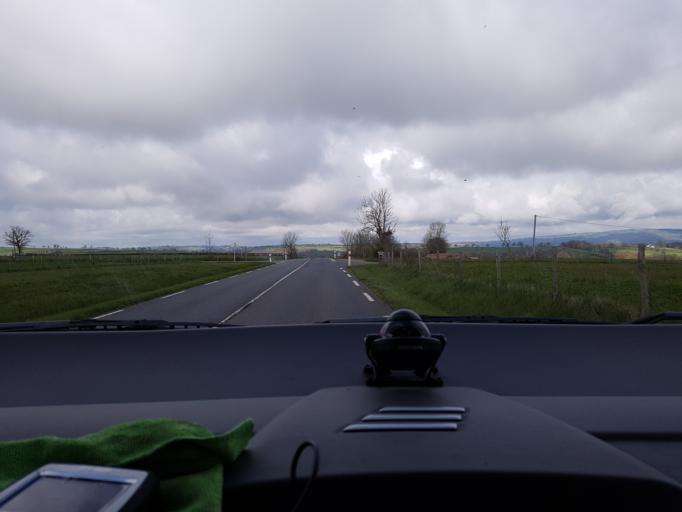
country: FR
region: Midi-Pyrenees
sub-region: Departement de l'Aveyron
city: Druelle
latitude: 44.3701
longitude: 2.4721
